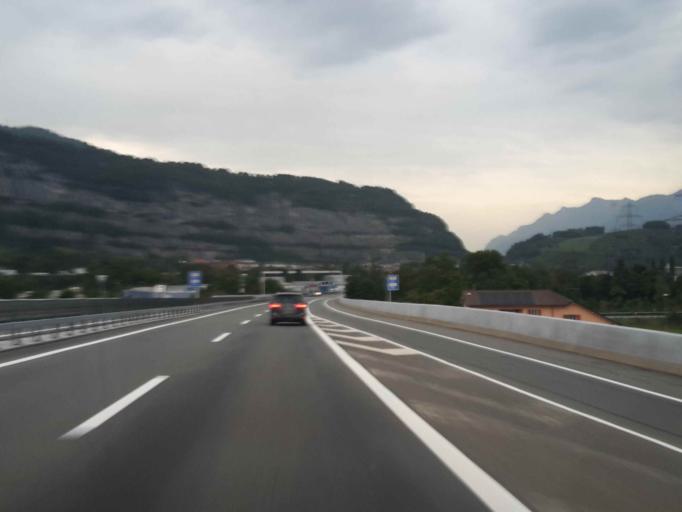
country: CH
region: Valais
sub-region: Saint-Maurice District
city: Saint-Maurice
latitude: 46.2017
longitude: 7.0145
